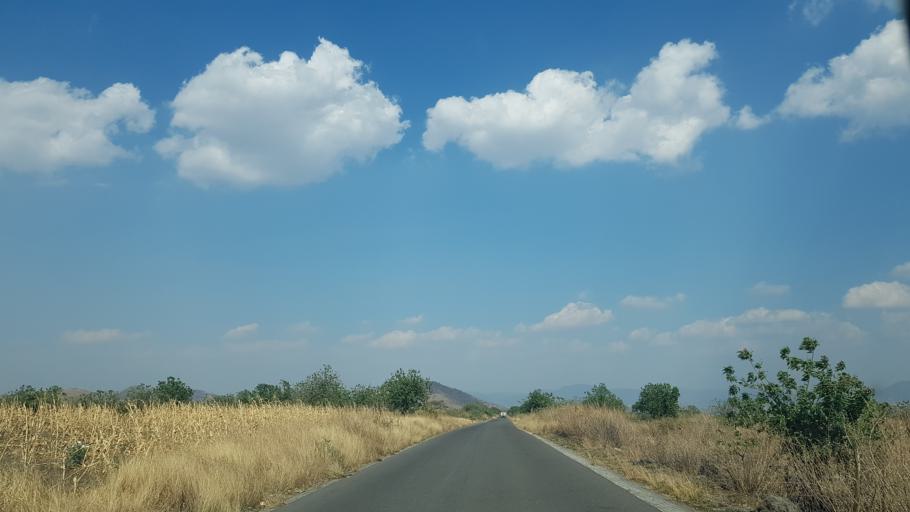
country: MX
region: Puebla
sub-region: Atlixco
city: Colonia Agricola de Ocotepec (Colonia San Jose)
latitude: 18.9235
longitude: -98.5058
